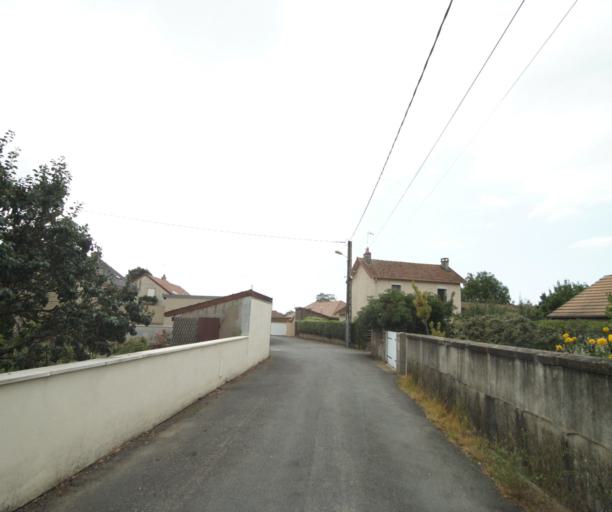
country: FR
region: Bourgogne
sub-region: Departement de Saone-et-Loire
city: Gueugnon
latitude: 46.6043
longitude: 4.0557
